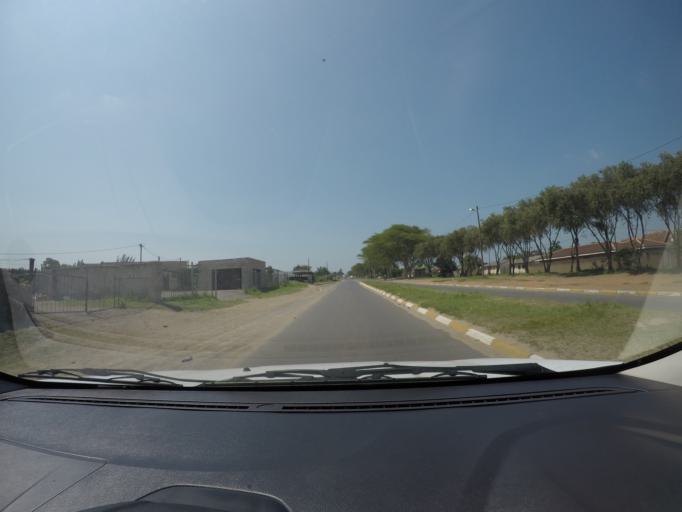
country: ZA
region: KwaZulu-Natal
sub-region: uThungulu District Municipality
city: eSikhawini
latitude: -28.8585
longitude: 31.9238
